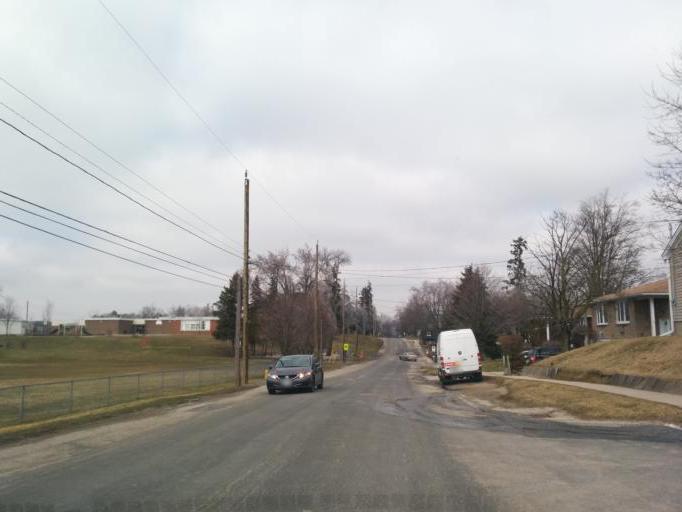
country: CA
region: Ontario
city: Waterloo
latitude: 43.5354
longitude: -80.5555
